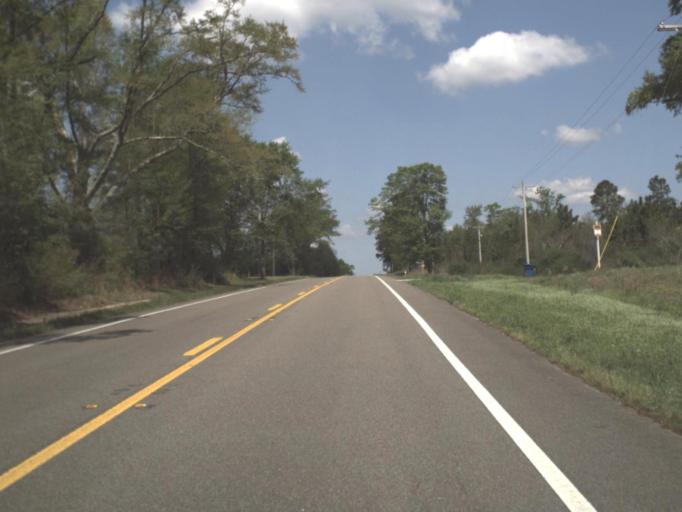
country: US
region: Alabama
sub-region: Escambia County
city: East Brewton
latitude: 30.9232
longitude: -87.0501
